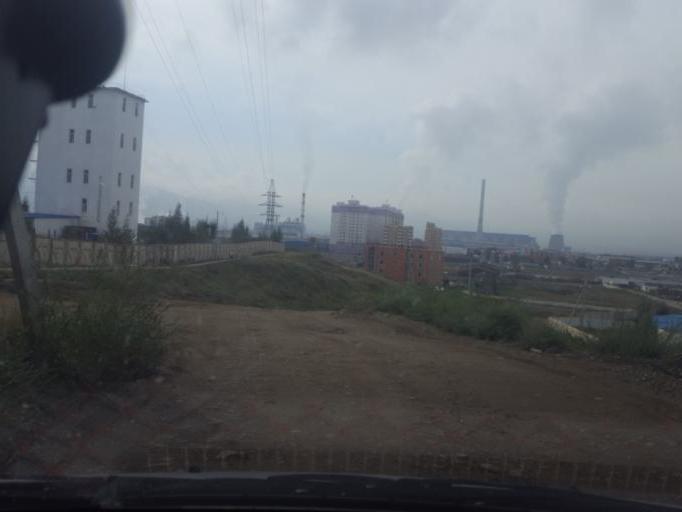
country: MN
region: Ulaanbaatar
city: Ulaanbaatar
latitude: 47.9167
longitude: 106.8004
